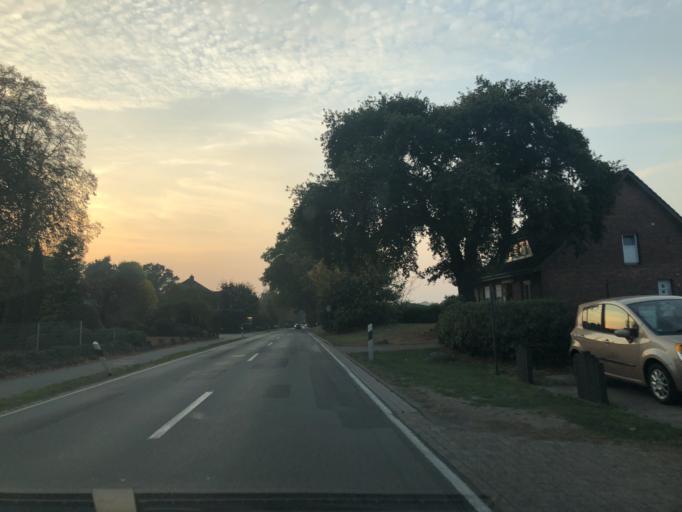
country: DE
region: Lower Saxony
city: Bosel
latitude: 53.0041
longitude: 7.9744
